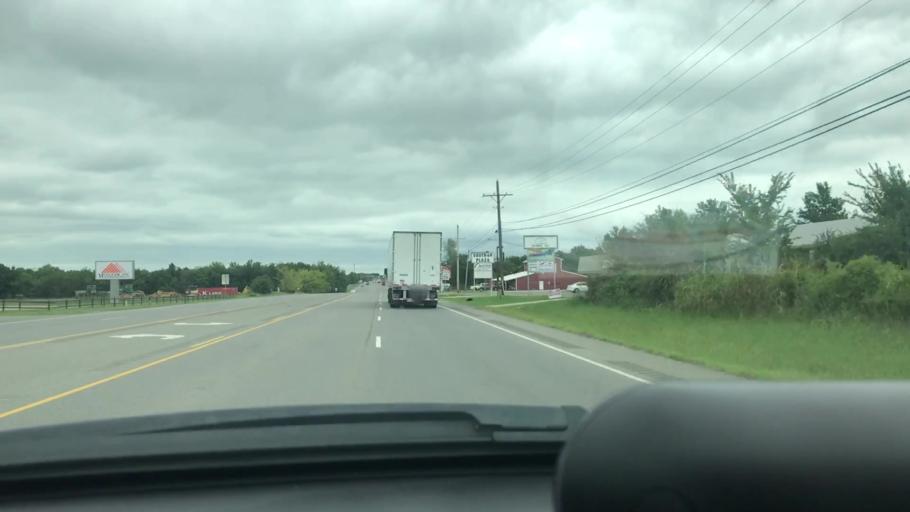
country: US
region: Oklahoma
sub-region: Wagoner County
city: Wagoner
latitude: 35.9368
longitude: -95.3952
